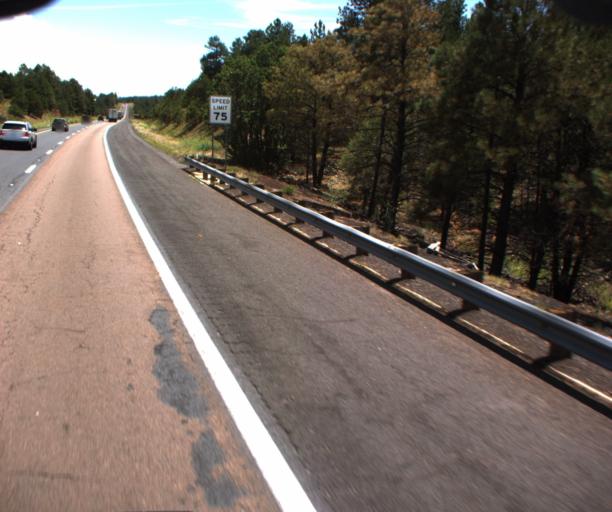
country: US
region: Arizona
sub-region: Coconino County
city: Parks
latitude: 35.2566
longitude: -111.9260
